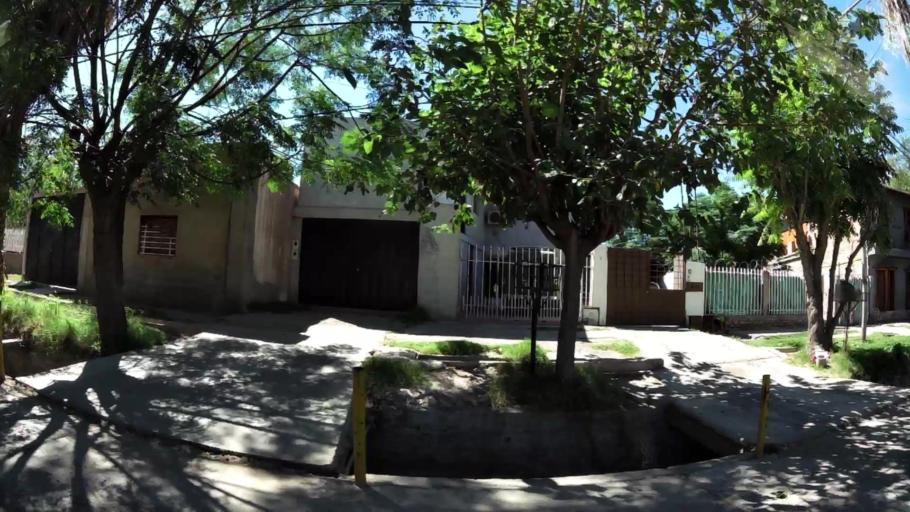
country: AR
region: Mendoza
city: Las Heras
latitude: -32.8320
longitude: -68.8381
